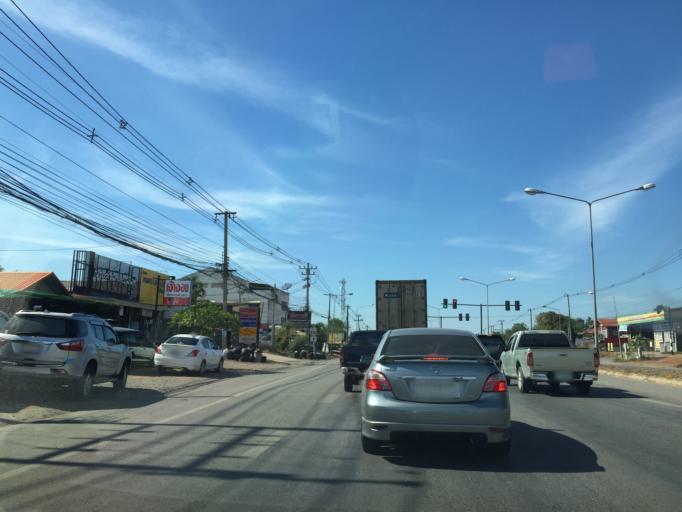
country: TH
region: Changwat Nong Bua Lamphu
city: Na Klang
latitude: 17.3092
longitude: 102.1795
